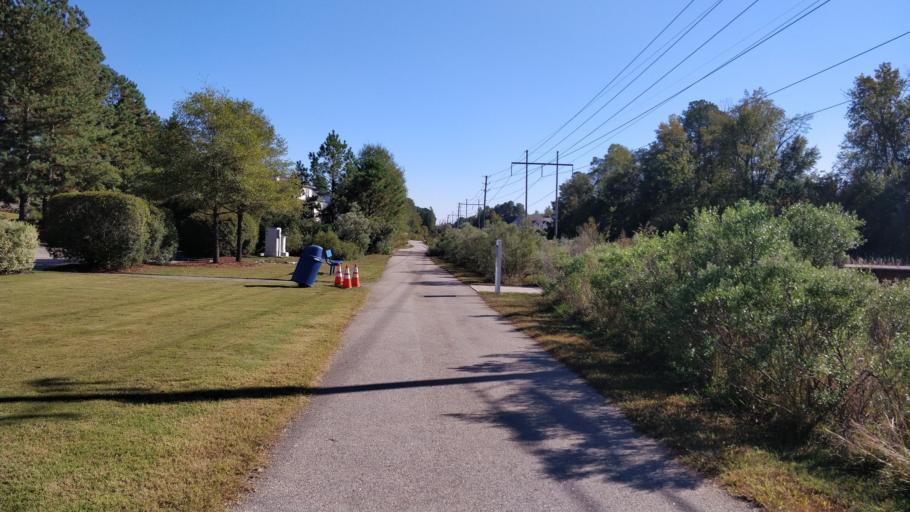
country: US
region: North Carolina
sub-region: Wake County
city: Morrisville
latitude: 35.8382
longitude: -78.8439
